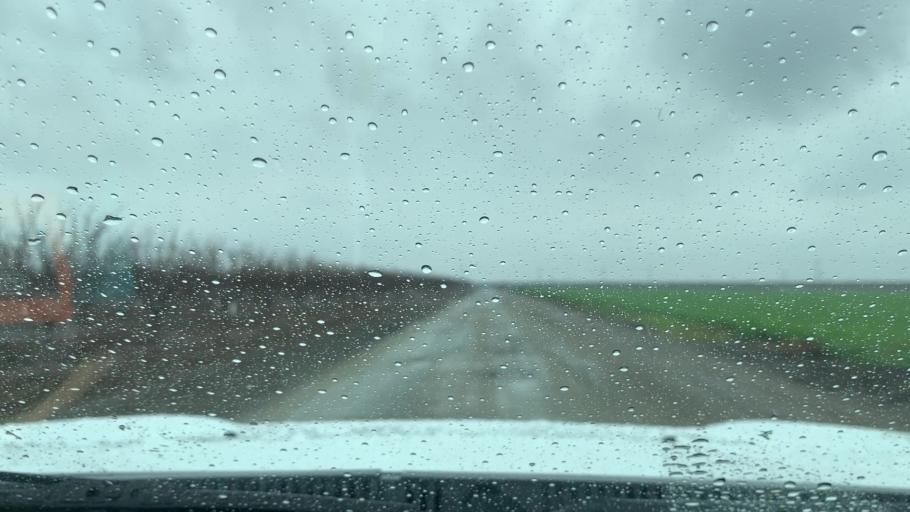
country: US
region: California
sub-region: Kings County
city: Corcoran
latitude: 36.0260
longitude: -119.5005
